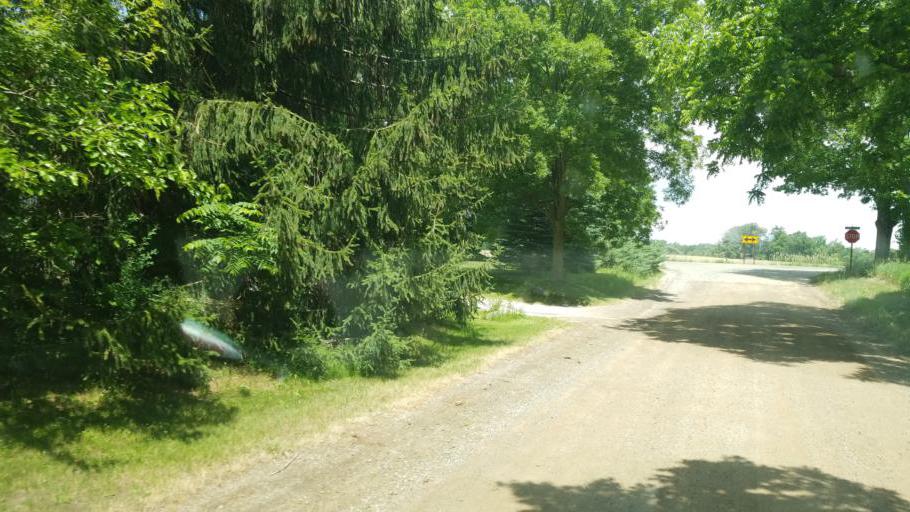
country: US
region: Michigan
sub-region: Eaton County
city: Charlotte
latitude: 42.6256
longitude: -84.8855
